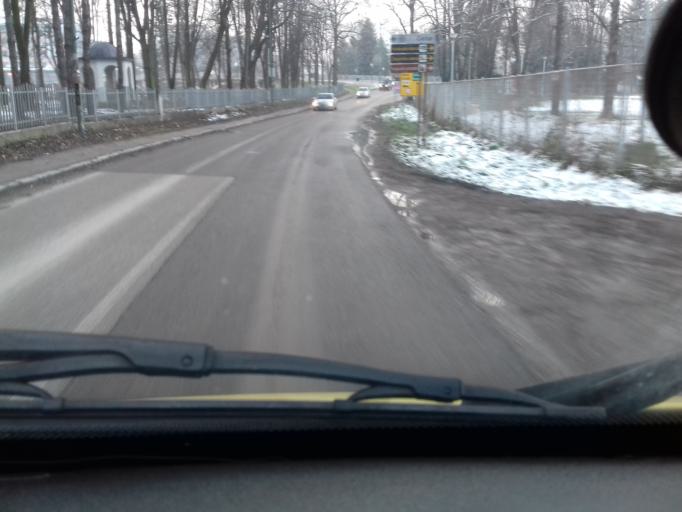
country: BA
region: Federation of Bosnia and Herzegovina
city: Visoko
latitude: 43.9896
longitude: 18.1854
